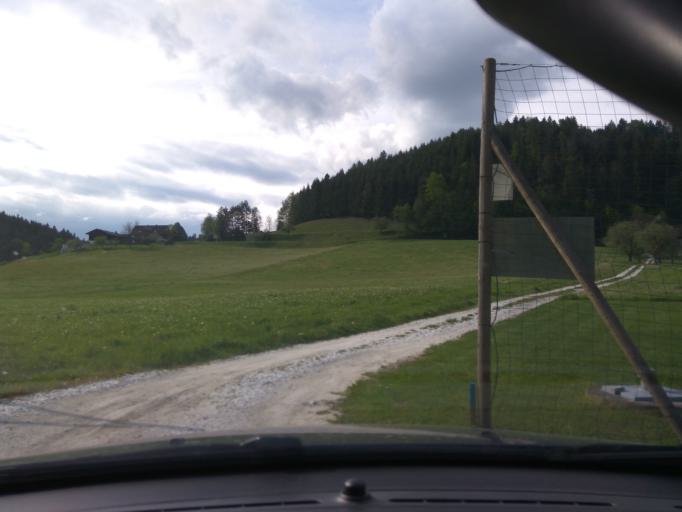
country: AT
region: Styria
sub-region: Politischer Bezirk Voitsberg
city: Voitsberg
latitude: 47.0287
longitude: 15.1178
